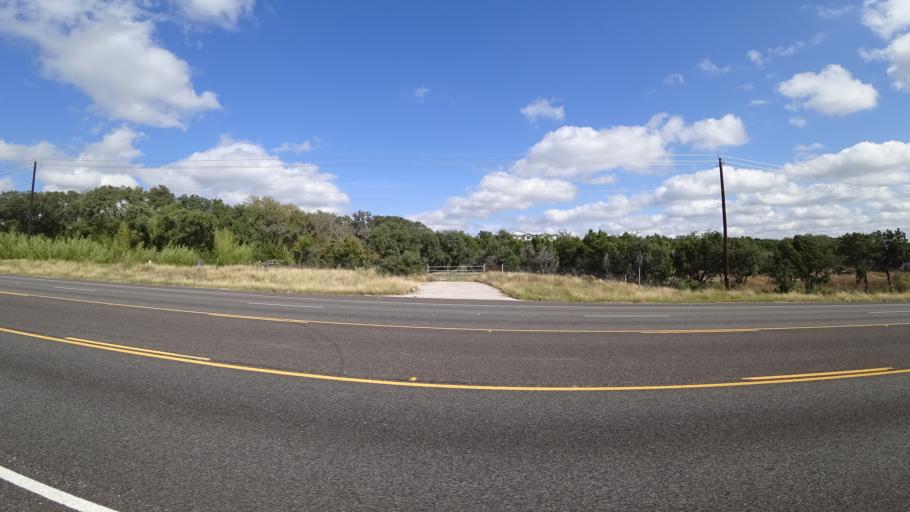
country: US
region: Texas
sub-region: Travis County
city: Barton Creek
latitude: 30.2577
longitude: -97.9052
